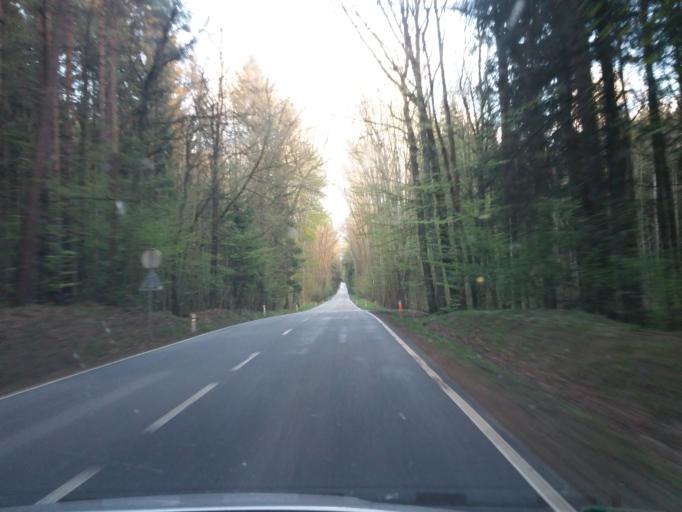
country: CZ
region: South Moravian
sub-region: Okres Blansko
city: Boskovice
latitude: 49.4790
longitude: 16.6916
